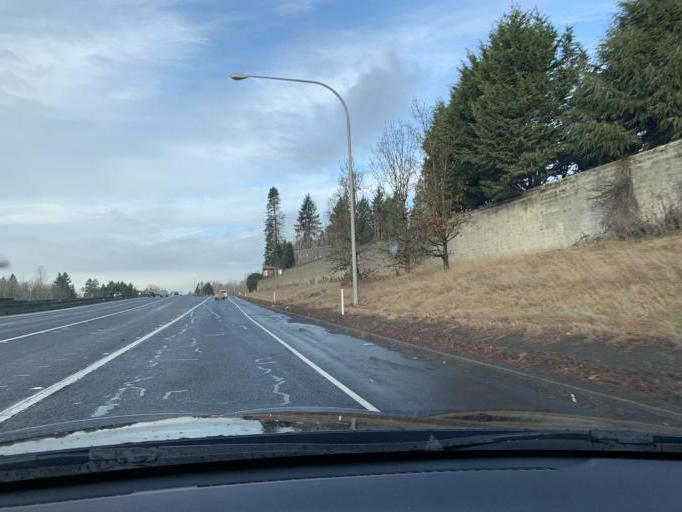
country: US
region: Washington
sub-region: Clark County
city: Mill Plain
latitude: 45.5905
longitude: -122.4987
